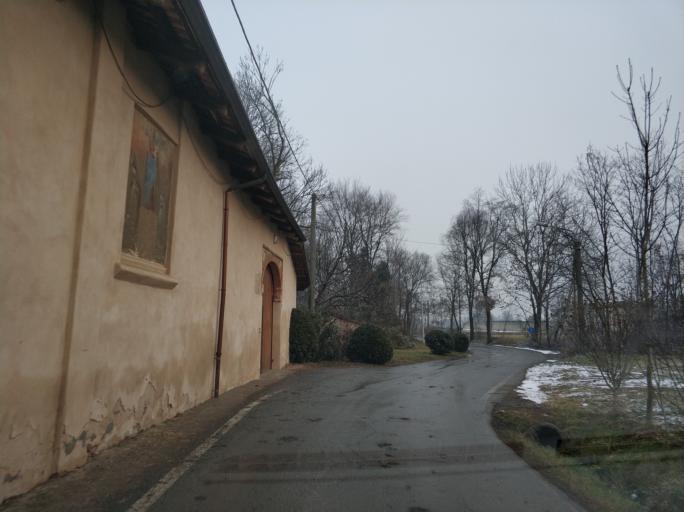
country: IT
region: Piedmont
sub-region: Provincia di Torino
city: San Francesco al Campo
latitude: 45.2245
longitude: 7.6689
